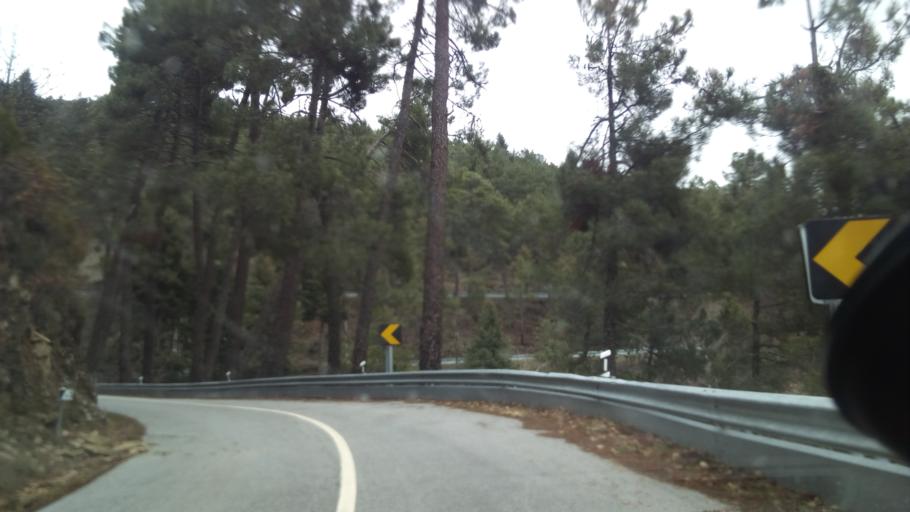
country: PT
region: Guarda
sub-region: Manteigas
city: Manteigas
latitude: 40.4158
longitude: -7.5326
